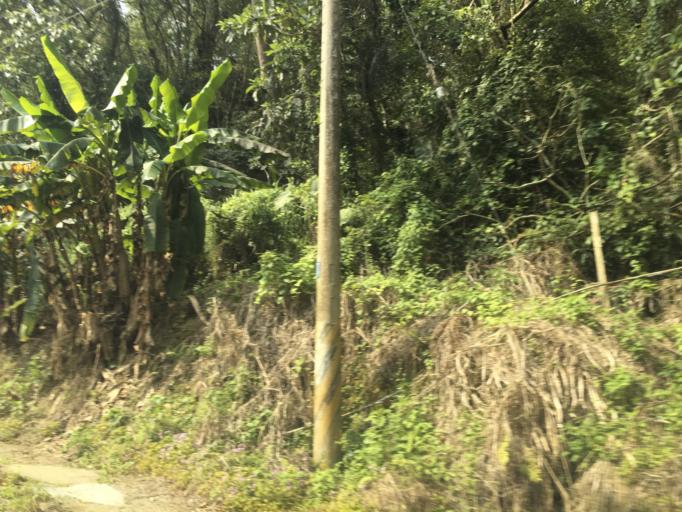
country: TW
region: Taiwan
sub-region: Taichung City
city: Taichung
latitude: 24.1339
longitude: 120.8241
